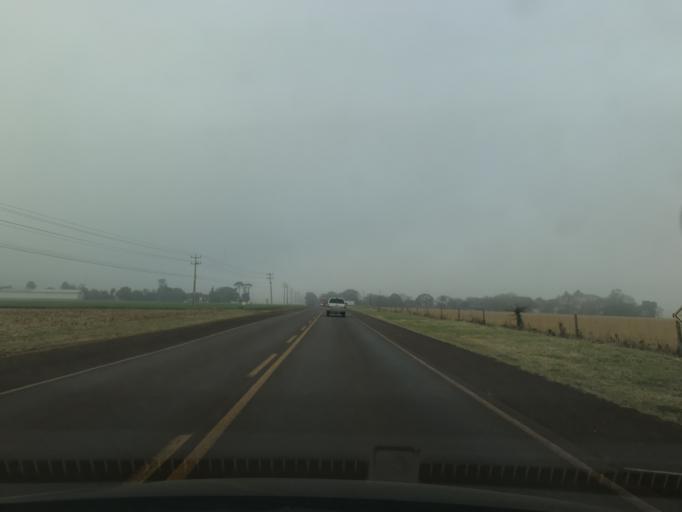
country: BR
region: Parana
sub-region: Toledo
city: Toledo
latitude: -24.6953
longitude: -53.6967
